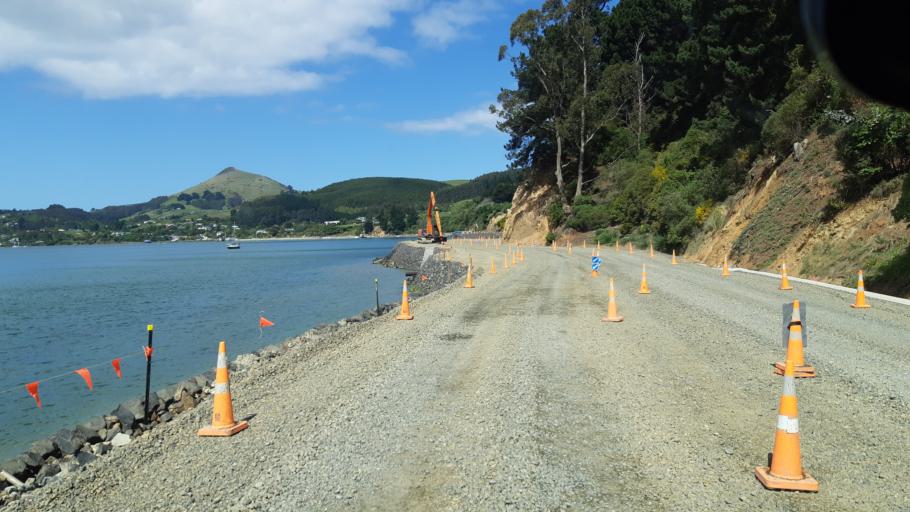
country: NZ
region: Otago
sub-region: Dunedin City
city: Portobello
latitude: -45.8451
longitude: 170.6059
